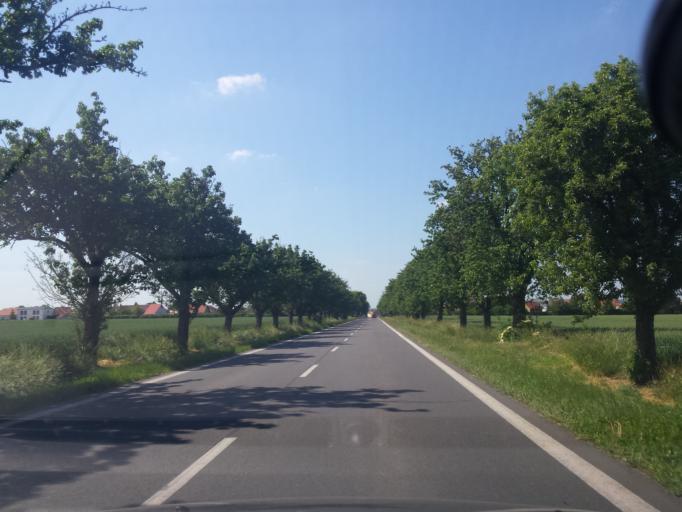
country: CZ
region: Central Bohemia
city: Horomerice
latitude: 50.1281
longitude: 14.3450
